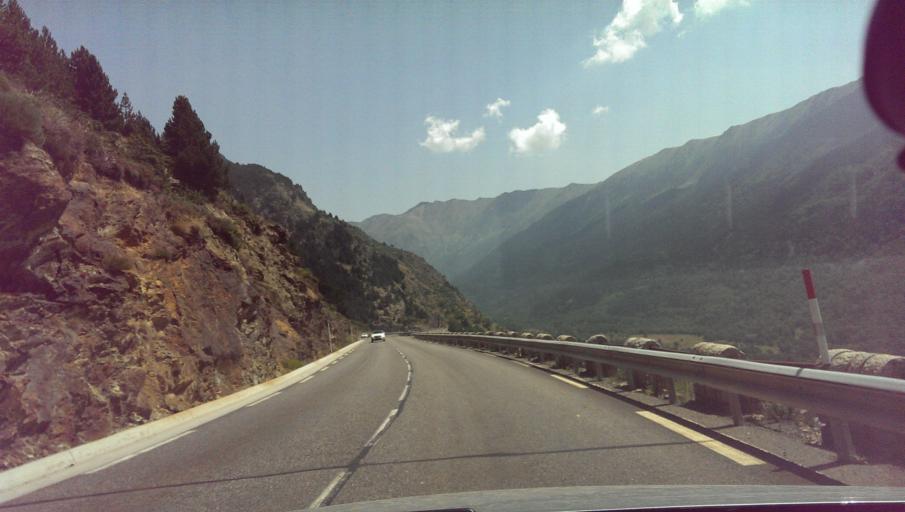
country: AD
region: Encamp
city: Pas de la Casa
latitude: 42.5512
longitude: 1.8266
